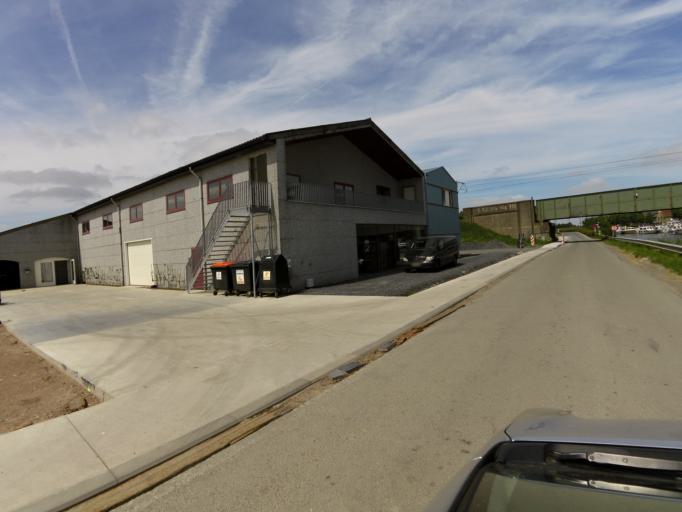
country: BE
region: Flanders
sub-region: Provincie West-Vlaanderen
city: Diksmuide
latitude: 51.0295
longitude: 2.8541
